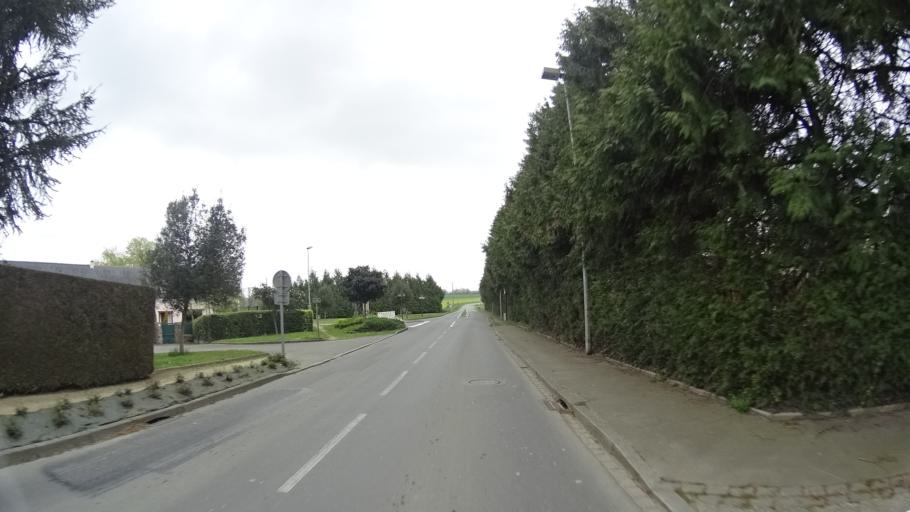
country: FR
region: Brittany
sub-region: Departement d'Ille-et-Vilaine
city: Cintre
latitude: 48.1021
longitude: -1.8683
